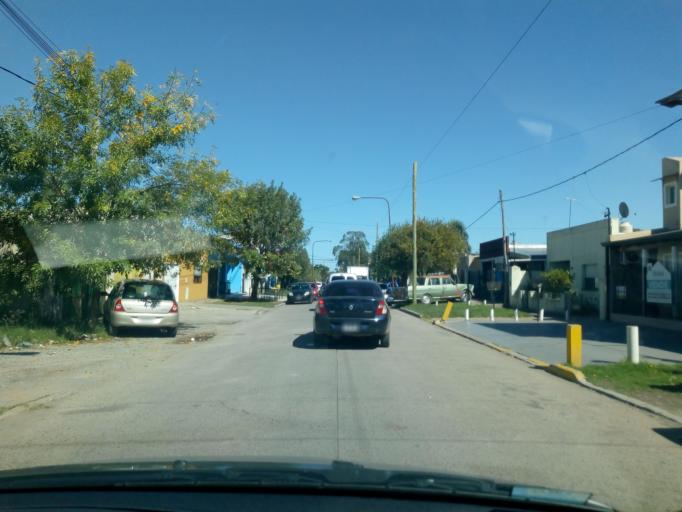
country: AR
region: Buenos Aires
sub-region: Partido de La Plata
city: La Plata
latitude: -34.9988
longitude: -58.0438
